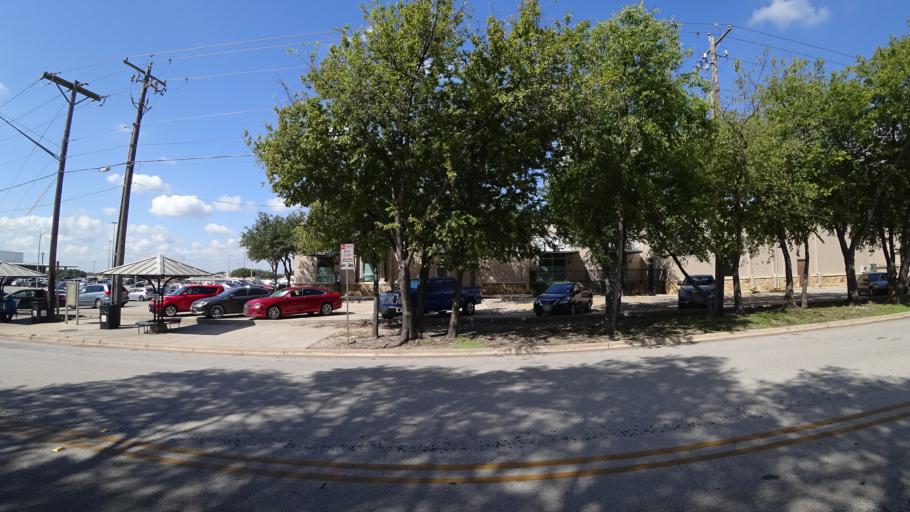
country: US
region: Texas
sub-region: Travis County
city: Austin
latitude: 30.3289
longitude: -97.7129
